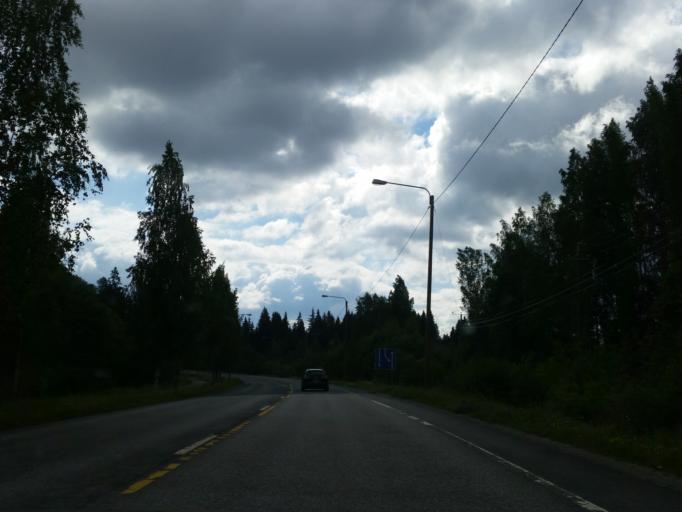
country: FI
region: Northern Savo
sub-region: Kuopio
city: Kuopio
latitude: 62.8394
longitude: 27.5599
